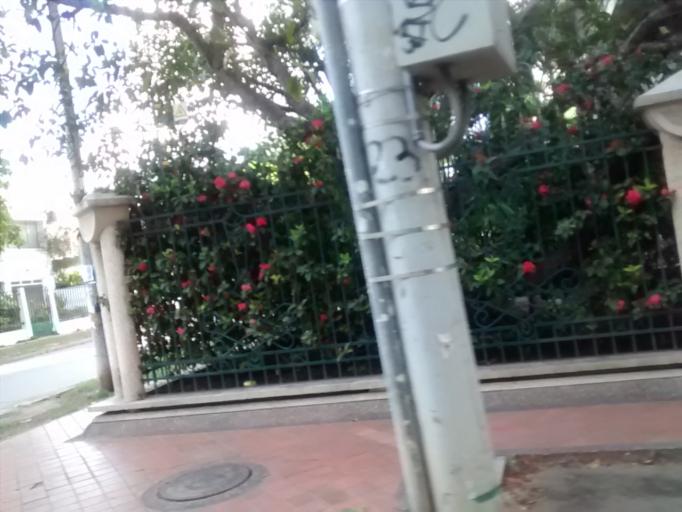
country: CO
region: Bolivar
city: Cartagena
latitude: 10.3959
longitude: -75.5538
